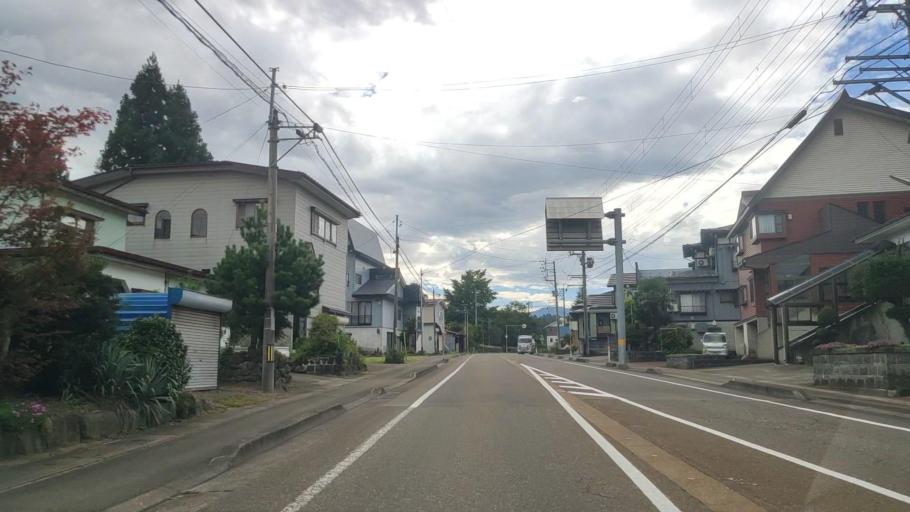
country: JP
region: Niigata
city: Arai
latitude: 36.9865
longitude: 138.2719
